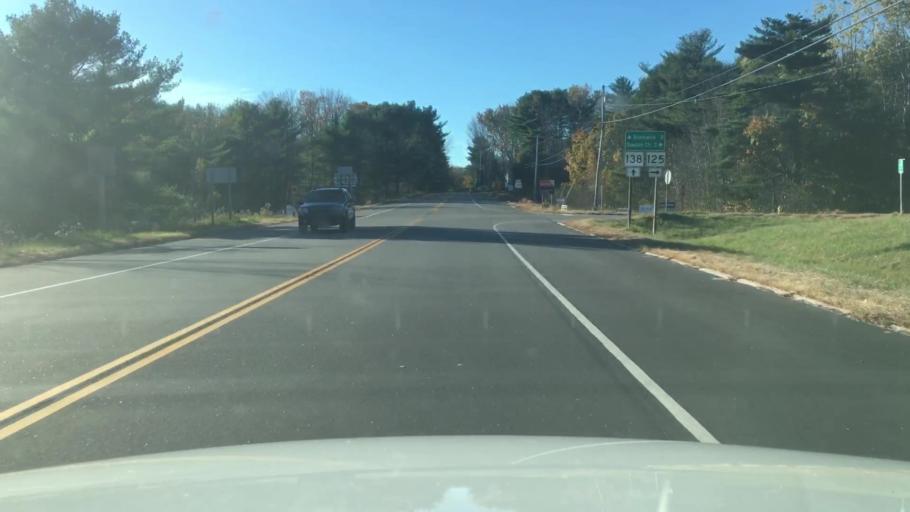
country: US
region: Maine
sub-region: Sagadahoc County
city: Topsham
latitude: 44.0175
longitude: -69.9221
